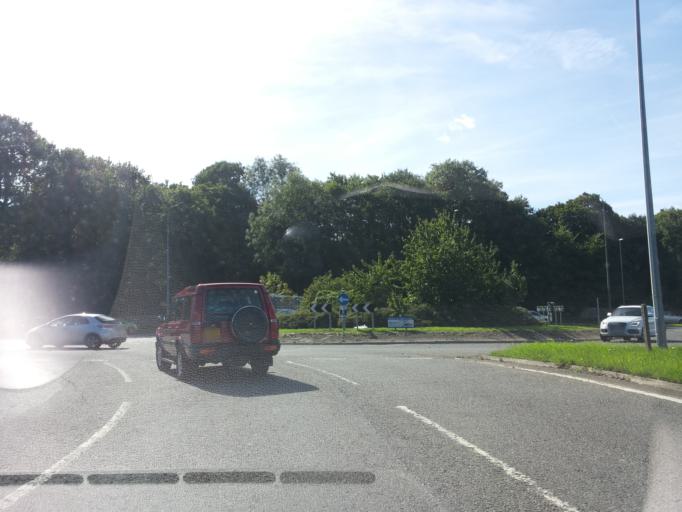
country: GB
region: England
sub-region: Kent
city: Boxley
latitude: 51.2846
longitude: 0.5492
